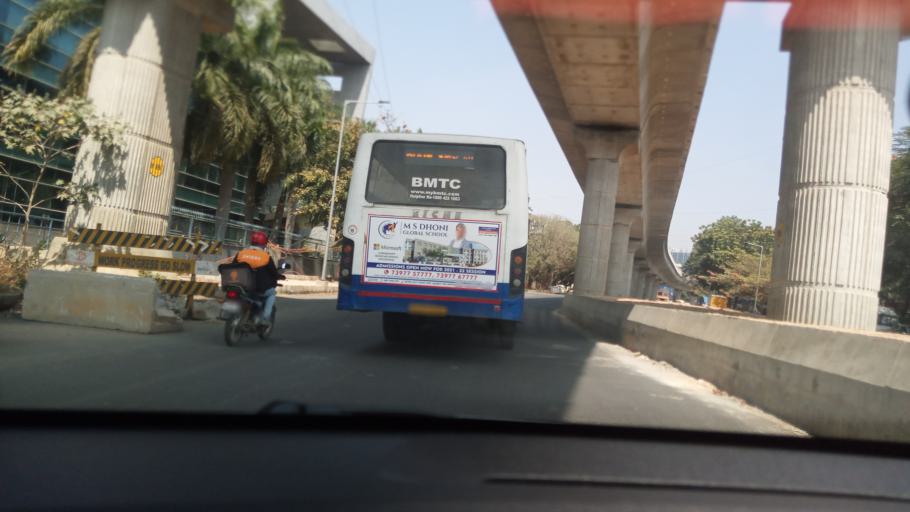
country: IN
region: Karnataka
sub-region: Bangalore Rural
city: Hoskote
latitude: 12.9834
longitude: 77.7284
